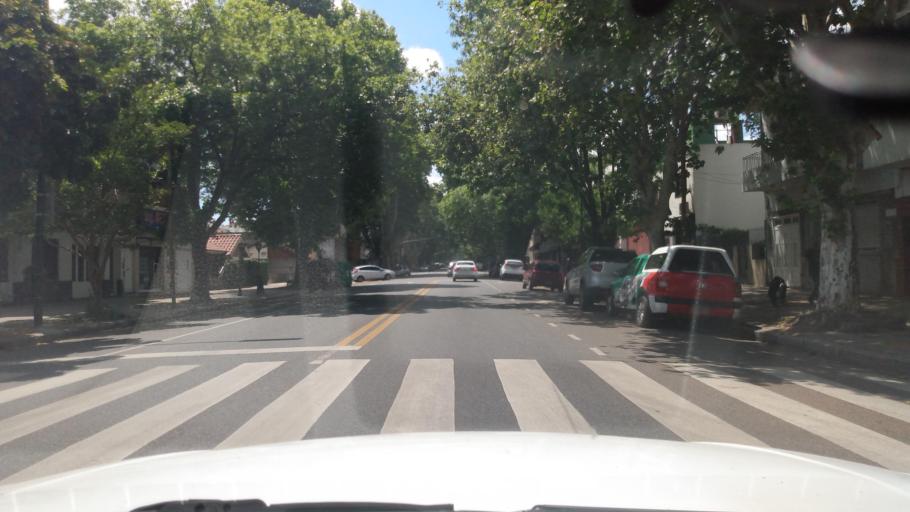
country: AR
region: Buenos Aires
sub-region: Partido de General San Martin
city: General San Martin
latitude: -34.5770
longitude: -58.5089
